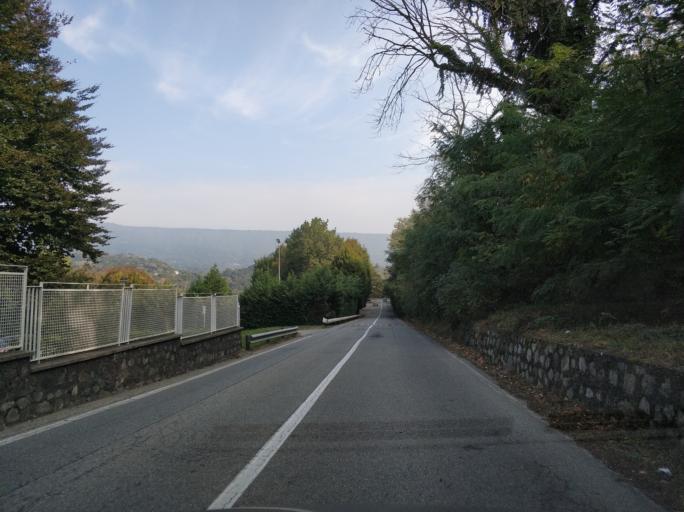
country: IT
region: Piedmont
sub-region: Provincia di Torino
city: Ivrea
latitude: 45.4815
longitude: 7.8800
